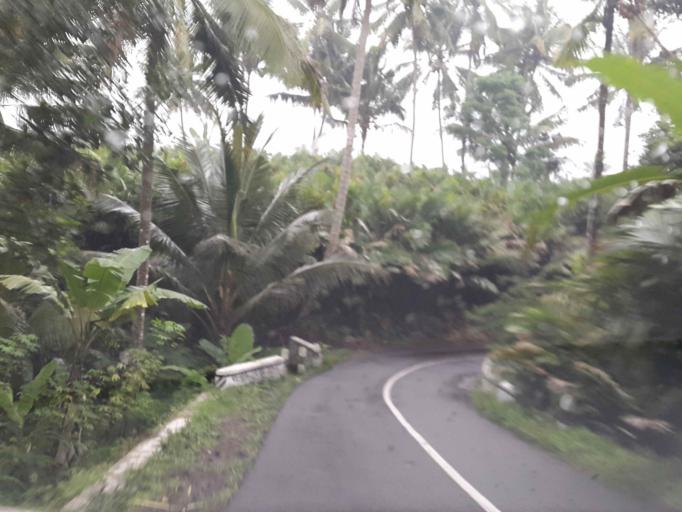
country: ID
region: Central Java
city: Muntilan
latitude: -7.5792
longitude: 110.3560
